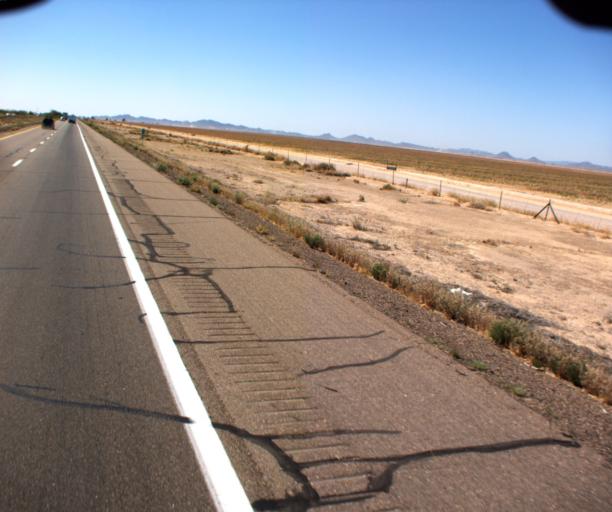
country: US
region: Arizona
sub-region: Maricopa County
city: Gila Bend
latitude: 32.9278
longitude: -112.8443
